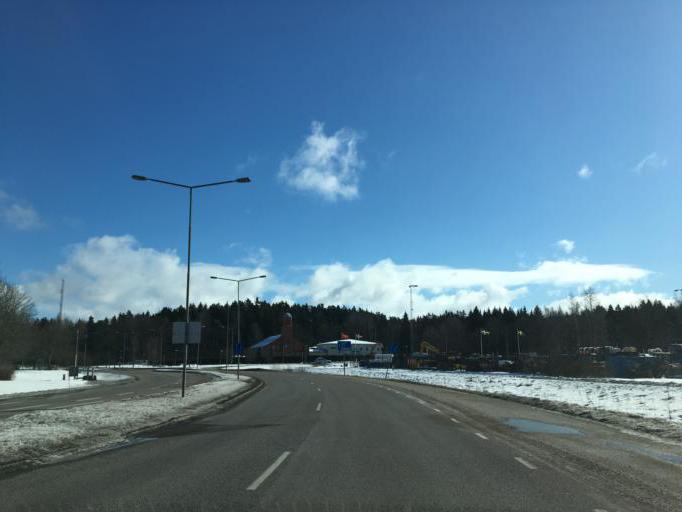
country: SE
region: Vaestmanland
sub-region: Vasteras
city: Vasteras
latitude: 59.6185
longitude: 16.5025
